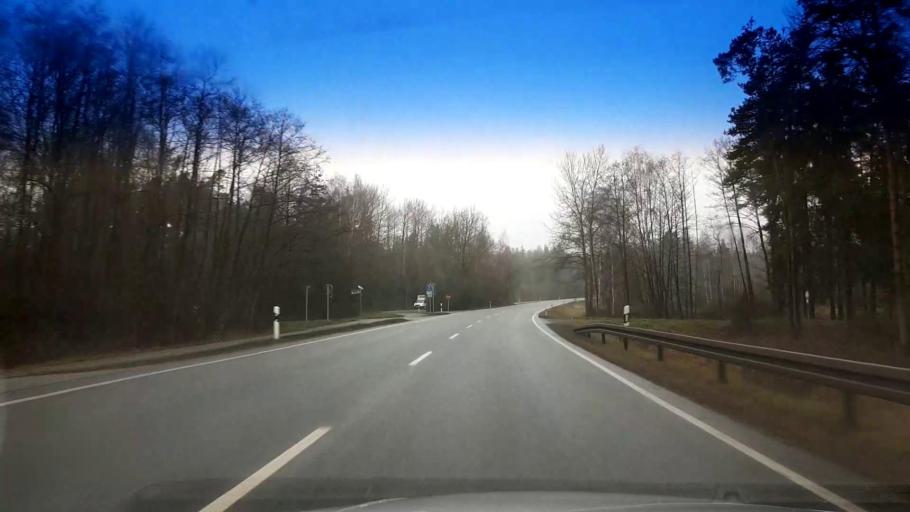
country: DE
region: Bavaria
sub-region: Upper Palatinate
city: Tirschenreuth
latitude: 49.8961
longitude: 12.3060
